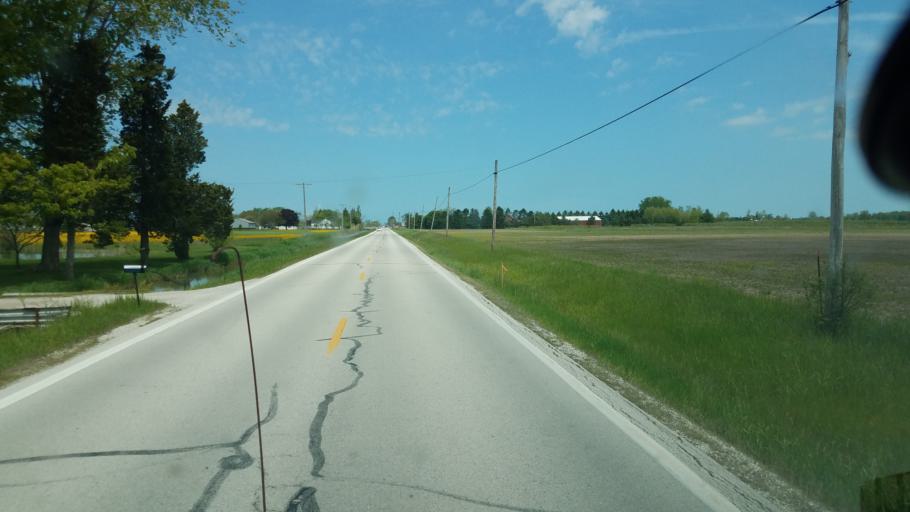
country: US
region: Ohio
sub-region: Ottawa County
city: Oak Harbor
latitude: 41.5704
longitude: -83.1449
